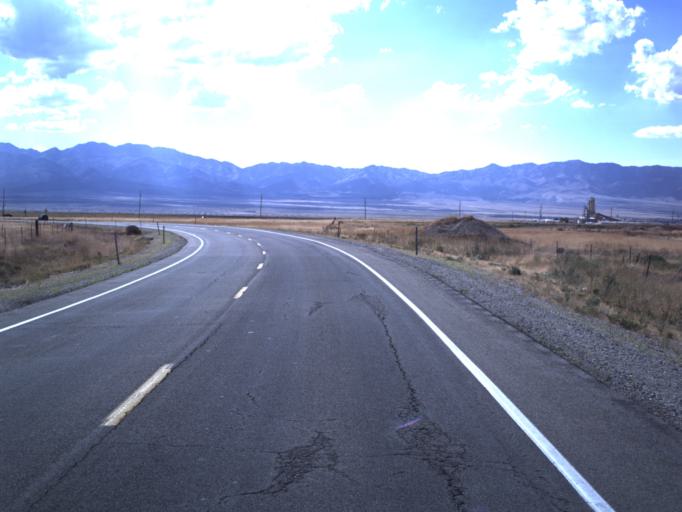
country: US
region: Utah
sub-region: Tooele County
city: Tooele
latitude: 40.5507
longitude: -112.3358
